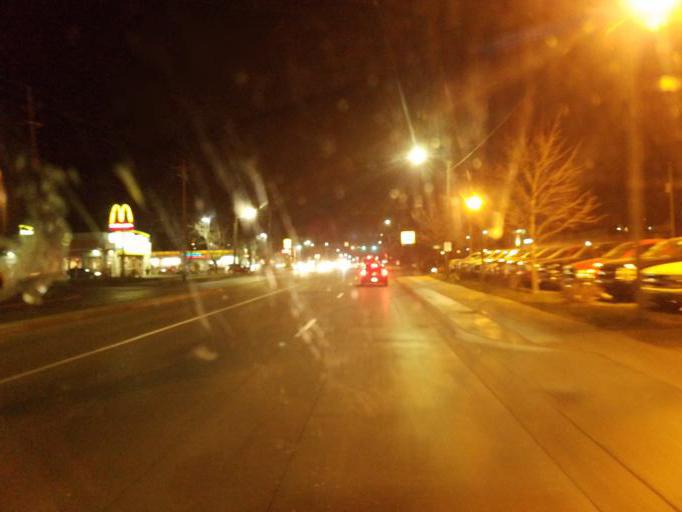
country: US
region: Iowa
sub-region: Polk County
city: Des Moines
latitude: 41.6004
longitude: -93.5699
